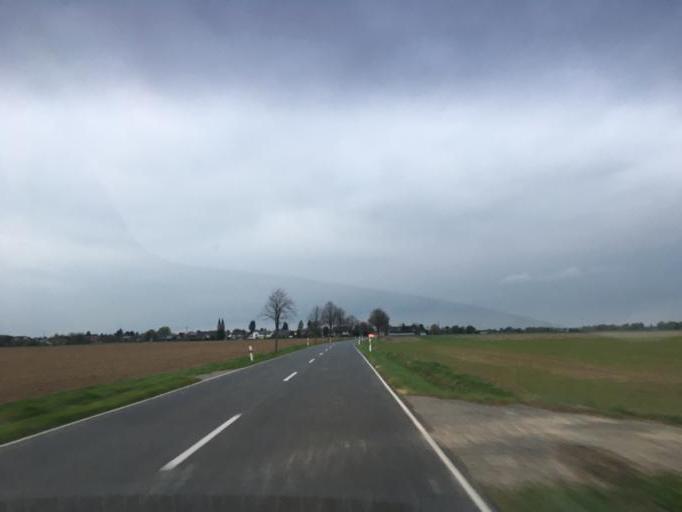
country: DE
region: North Rhine-Westphalia
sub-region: Regierungsbezirk Koln
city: Vettweiss
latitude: 50.7572
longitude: 6.5697
